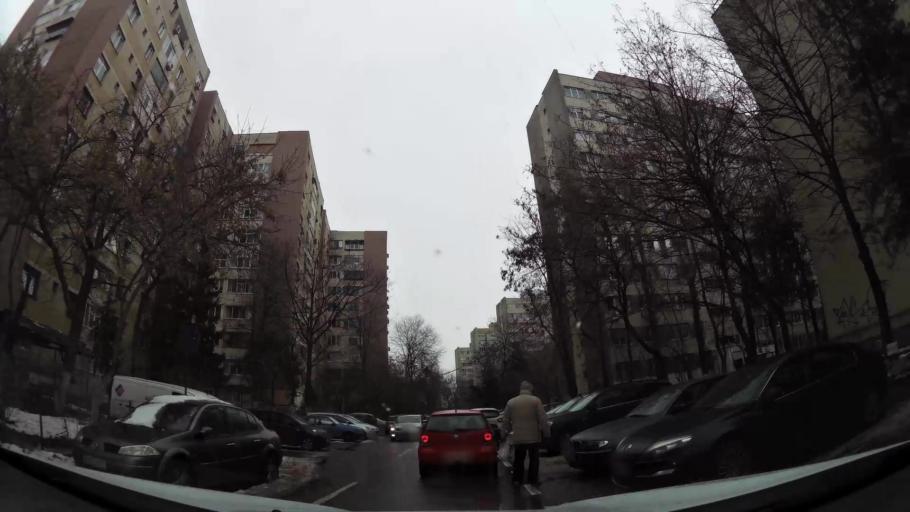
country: RO
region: Ilfov
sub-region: Comuna Chiajna
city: Rosu
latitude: 44.4186
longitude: 26.0241
